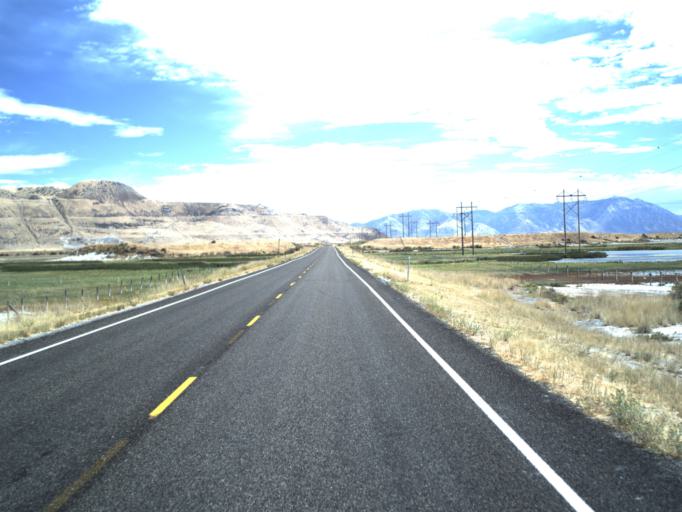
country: US
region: Utah
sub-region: Box Elder County
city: Tremonton
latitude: 41.6044
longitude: -112.3156
